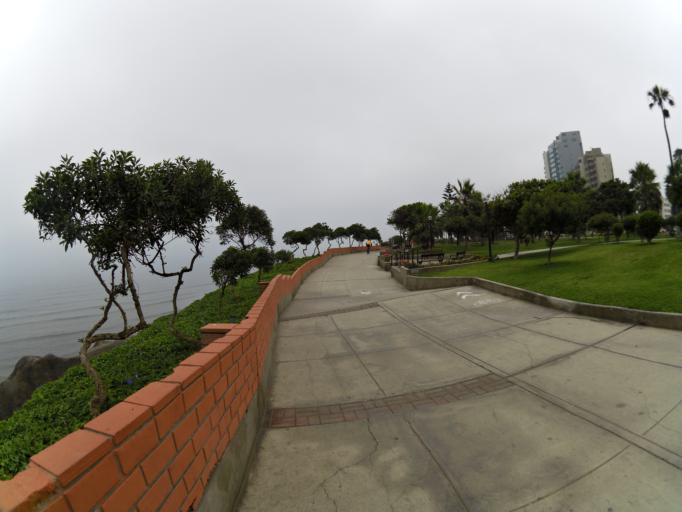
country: PE
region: Lima
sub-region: Lima
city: San Isidro
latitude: -12.1244
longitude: -77.0386
